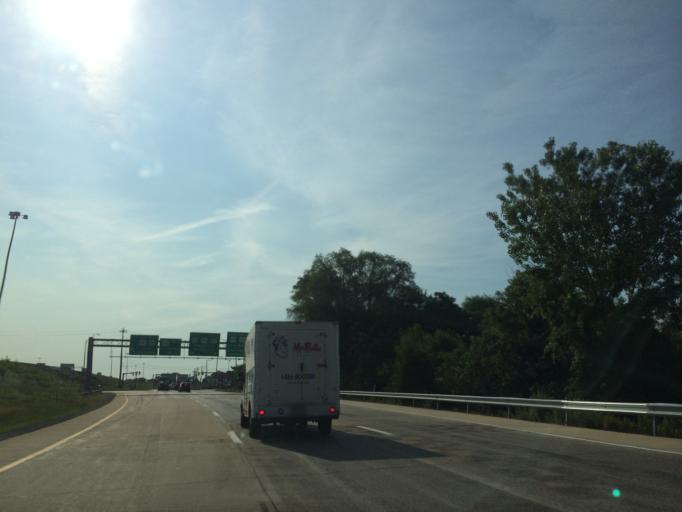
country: US
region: Pennsylvania
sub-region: Lancaster County
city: Lancaster
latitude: 40.0689
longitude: -76.3102
